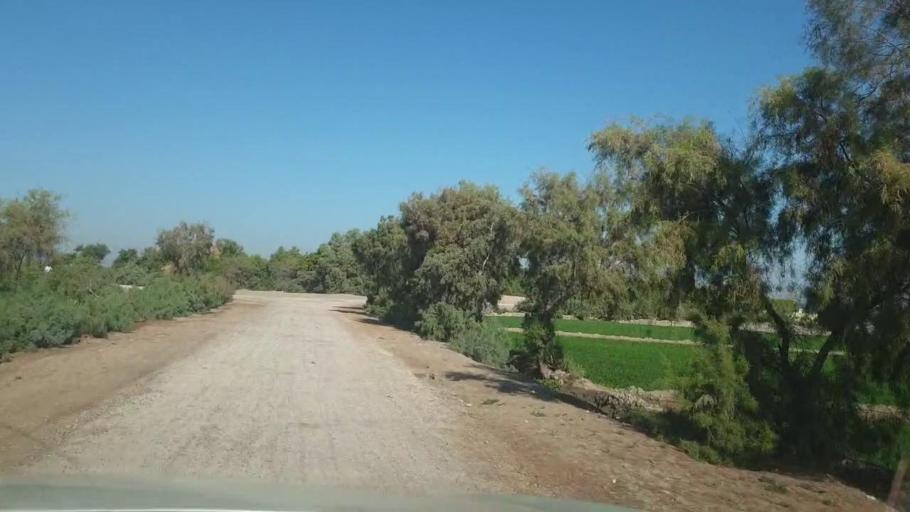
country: PK
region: Sindh
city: Bhan
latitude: 26.5284
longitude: 67.6429
